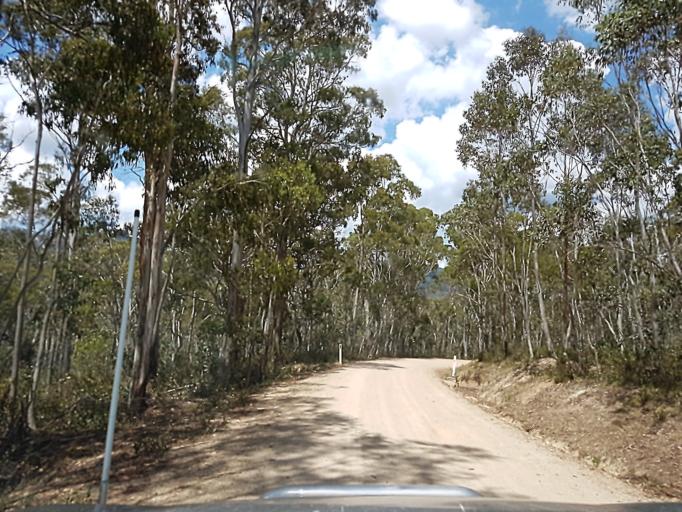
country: AU
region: New South Wales
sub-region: Snowy River
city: Jindabyne
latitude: -36.8819
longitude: 148.0861
